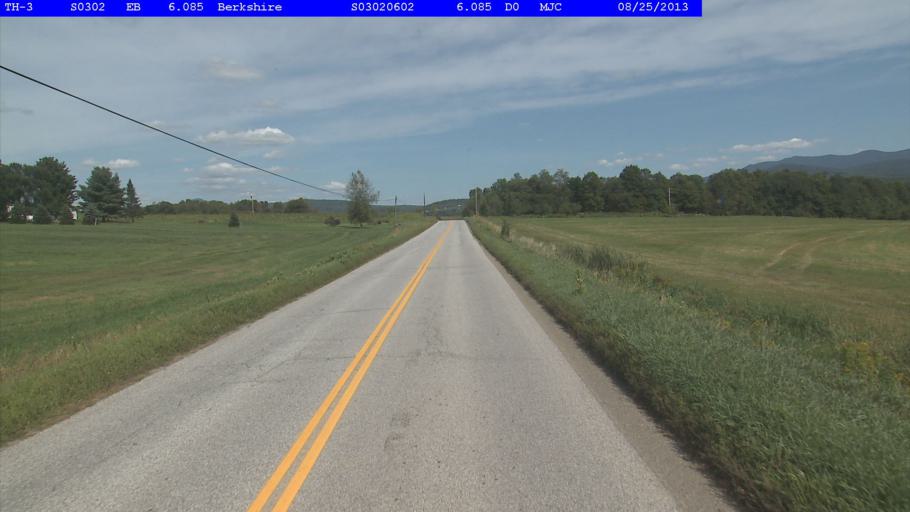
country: US
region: Vermont
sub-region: Franklin County
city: Richford
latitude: 44.9892
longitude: -72.7009
